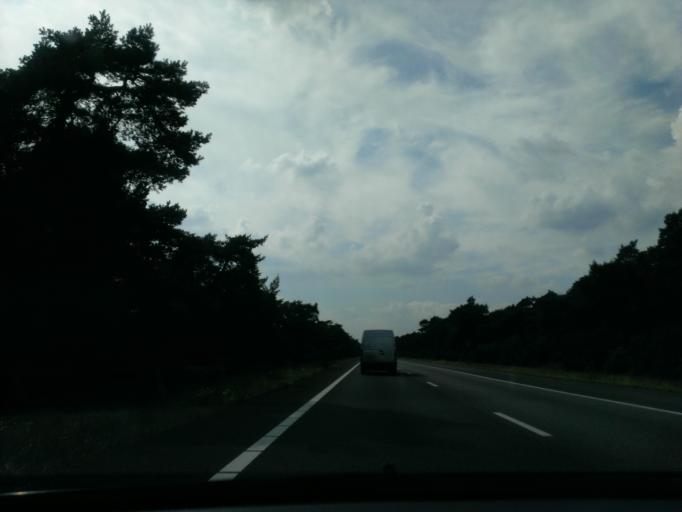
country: NL
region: Gelderland
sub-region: Gemeente Barneveld
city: Garderen
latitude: 52.1951
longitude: 5.7380
